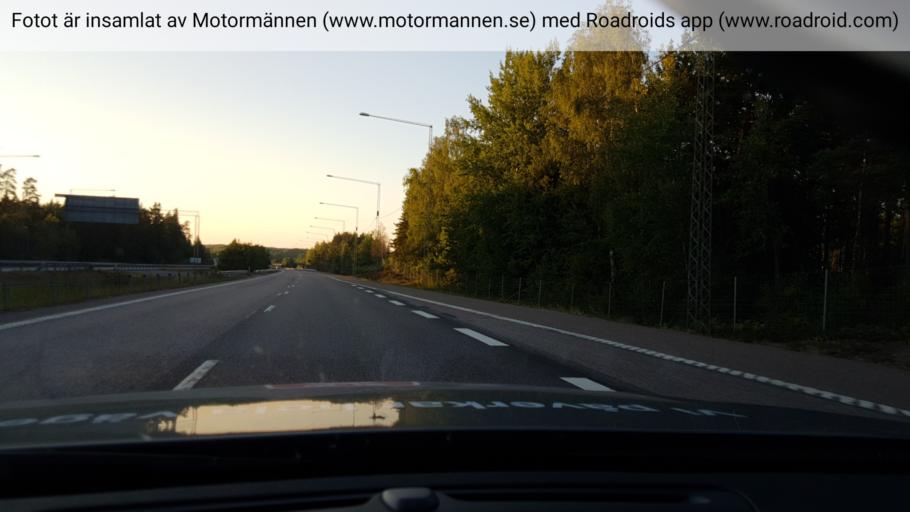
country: SE
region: Stockholm
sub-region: Sigtuna Kommun
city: Marsta
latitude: 59.6259
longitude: 17.9003
